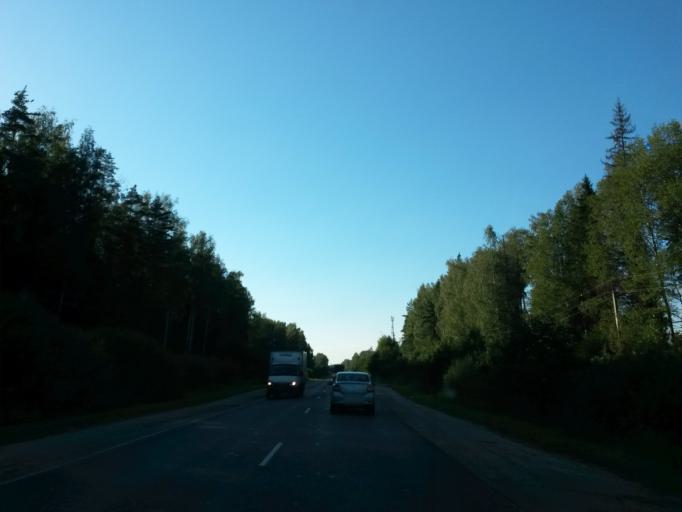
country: RU
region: Ivanovo
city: Novo-Talitsy
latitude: 57.0562
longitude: 40.7286
